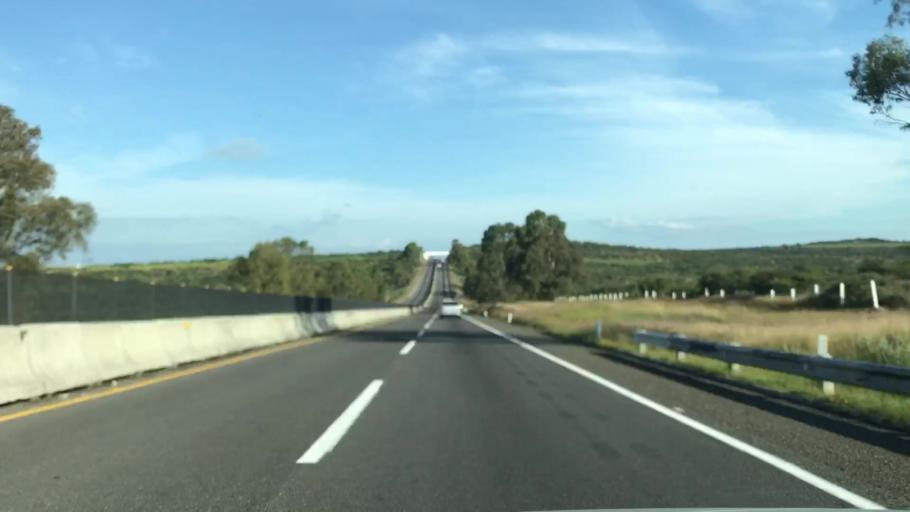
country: MX
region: Jalisco
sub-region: Lagos de Moreno
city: Cristeros [Fraccionamiento]
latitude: 21.3760
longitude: -102.1359
